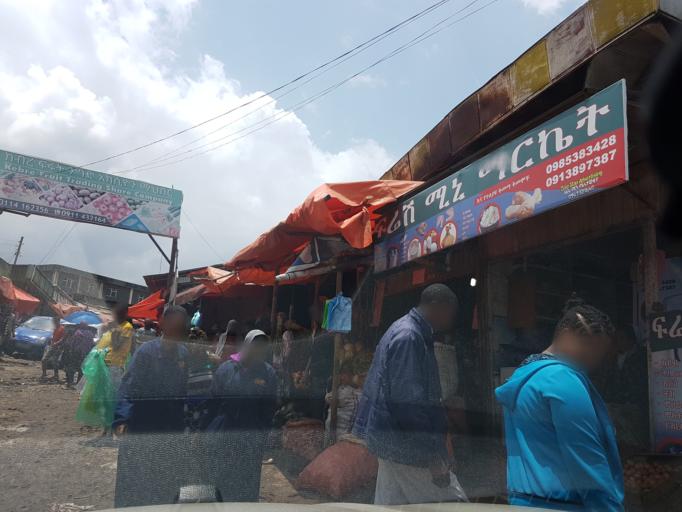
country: ET
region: Adis Abeba
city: Addis Ababa
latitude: 8.9857
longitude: 38.7491
